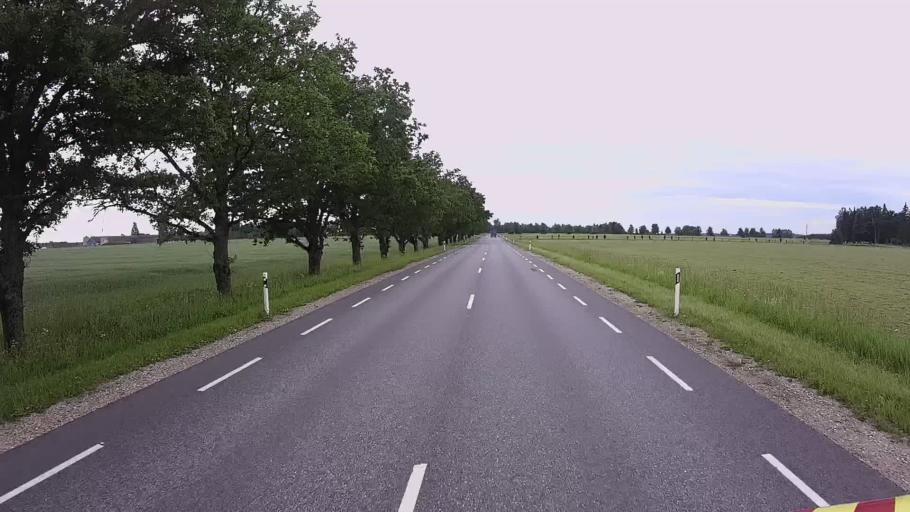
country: EE
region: Viljandimaa
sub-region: Karksi vald
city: Karksi-Nuia
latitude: 58.1303
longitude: 25.5825
